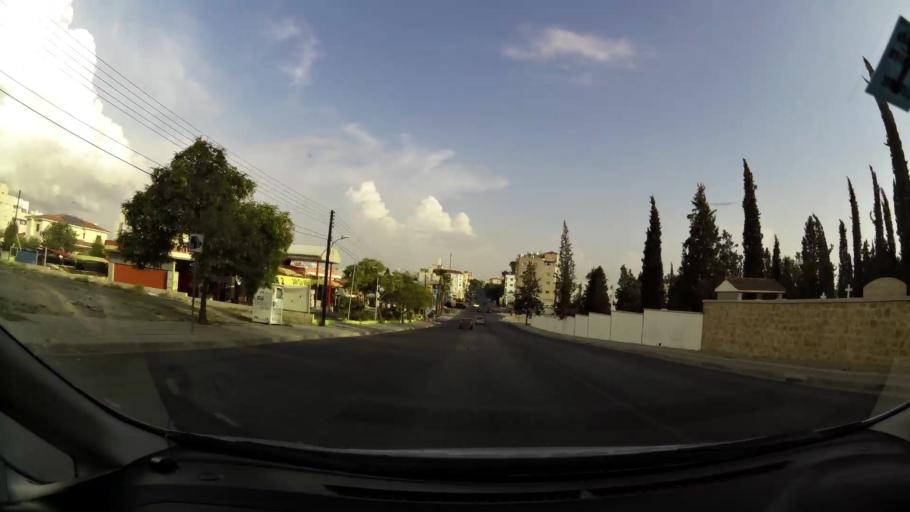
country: CY
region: Lefkosia
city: Nicosia
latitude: 35.1663
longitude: 33.3813
